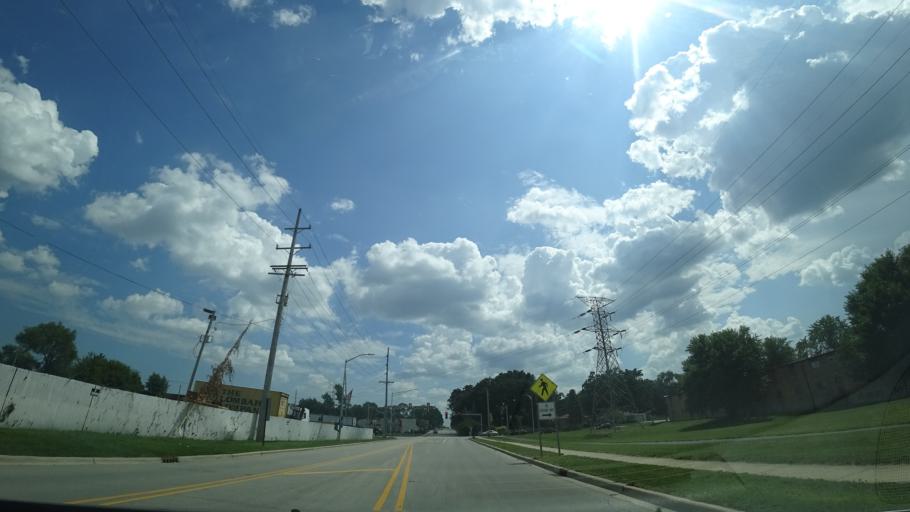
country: US
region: Illinois
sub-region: Cook County
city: Alsip
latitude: 41.6701
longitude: -87.7292
